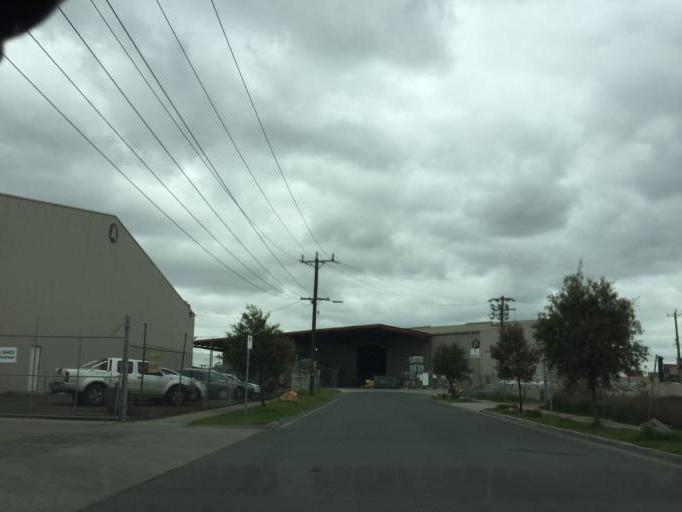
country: AU
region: Victoria
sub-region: Brimbank
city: Brooklyn
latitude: -37.8080
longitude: 144.8506
